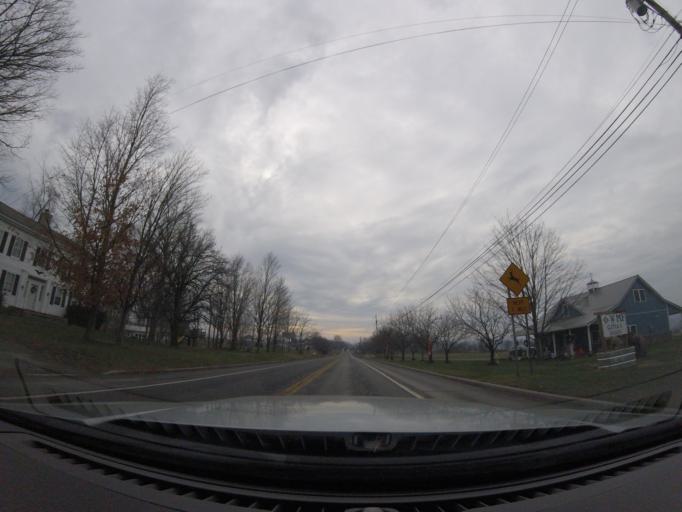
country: US
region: New York
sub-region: Schuyler County
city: Watkins Glen
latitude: 42.4125
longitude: -76.8513
